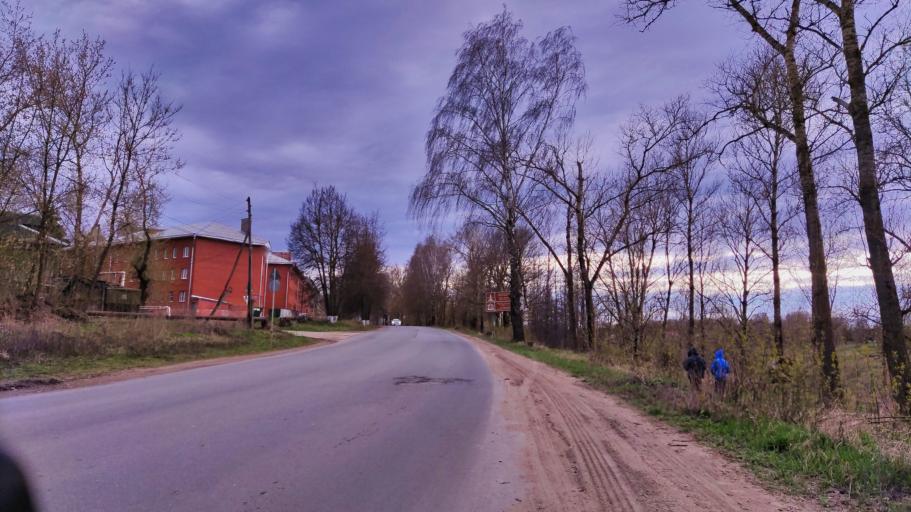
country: RU
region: Tverskaya
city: Rzhev
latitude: 56.2587
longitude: 34.3220
